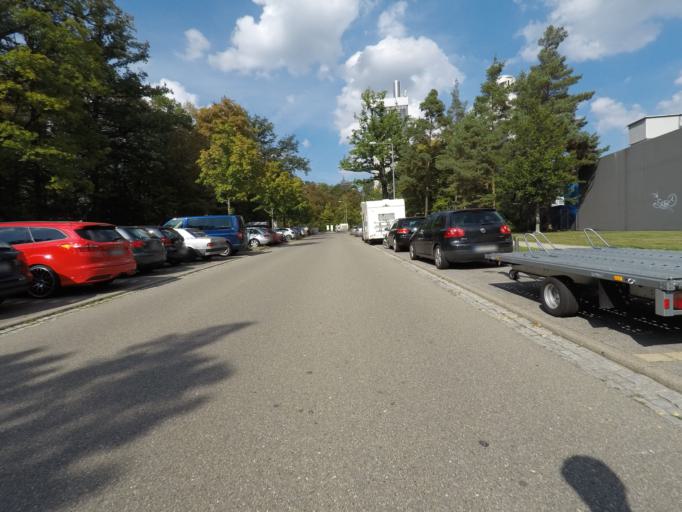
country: DE
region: Baden-Wuerttemberg
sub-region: Regierungsbezirk Stuttgart
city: Gerlingen
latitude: 48.7492
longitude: 9.1101
